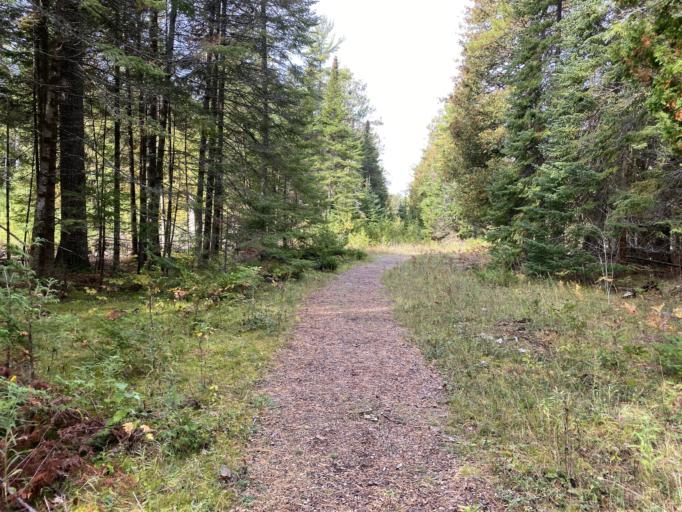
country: US
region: Michigan
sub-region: Mackinac County
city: Saint Ignace
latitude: 45.7513
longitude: -84.8794
